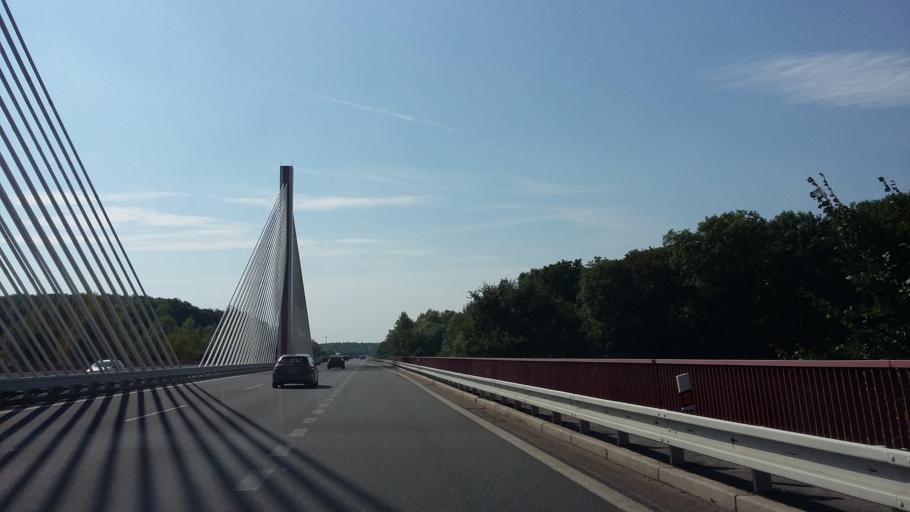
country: CZ
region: Central Bohemia
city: Libice nad Cidlinou
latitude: 50.1186
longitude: 15.1608
